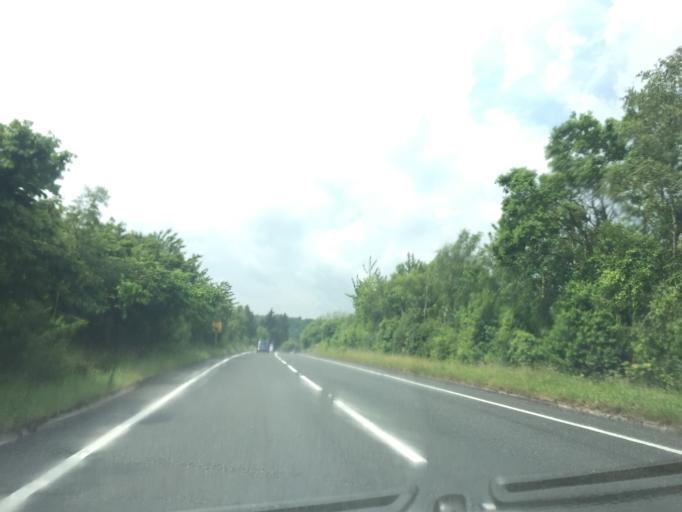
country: GB
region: England
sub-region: Dorset
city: Wareham
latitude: 50.6488
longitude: -2.0751
